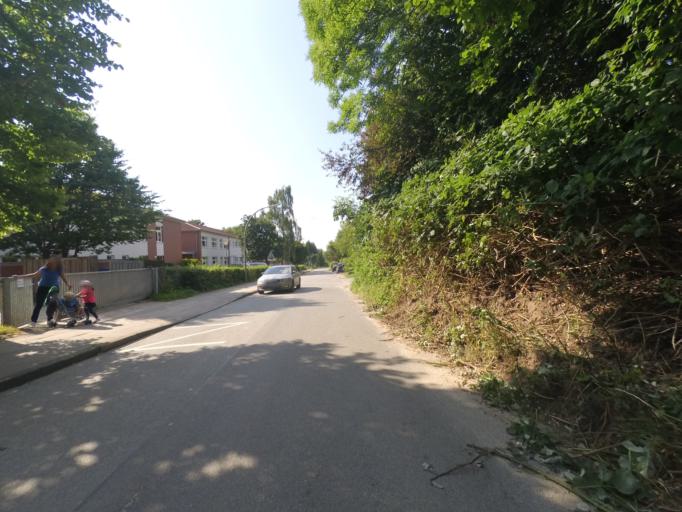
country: DE
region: Schleswig-Holstein
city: Oststeinbek
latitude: 53.5125
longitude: 10.1609
